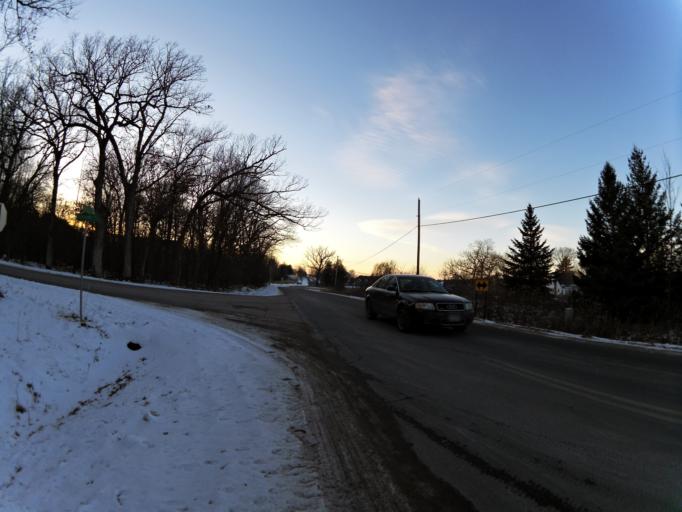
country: US
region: Minnesota
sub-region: Washington County
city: Lake Elmo
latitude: 44.9781
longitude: -92.8410
